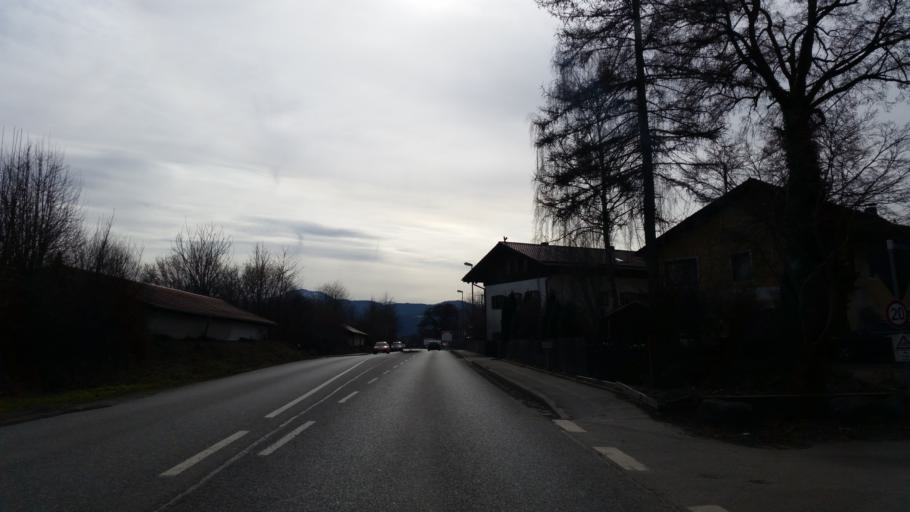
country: DE
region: Bavaria
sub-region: Upper Bavaria
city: Bad Aibling
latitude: 47.8457
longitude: 12.0135
